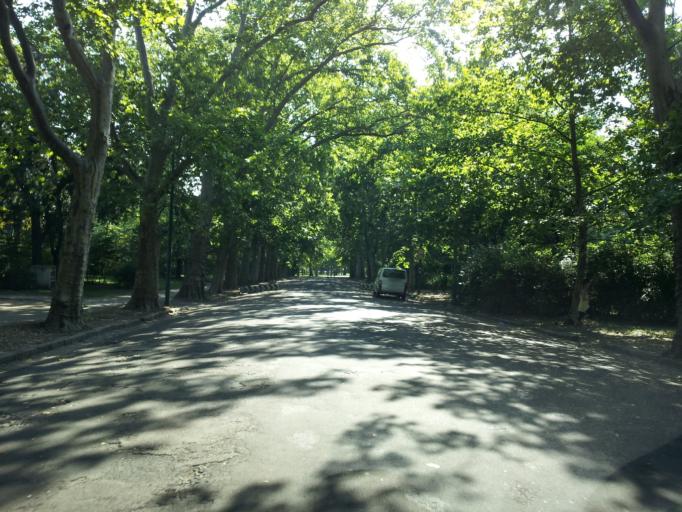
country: HU
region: Budapest
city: Budapest XIII. keruelet
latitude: 47.5166
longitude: 19.0841
